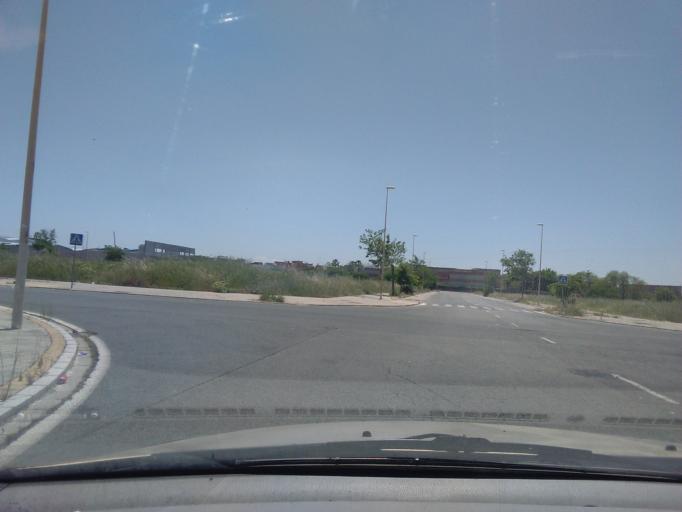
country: ES
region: Andalusia
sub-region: Provincia de Sevilla
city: Sevilla
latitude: 37.3791
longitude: -5.9318
